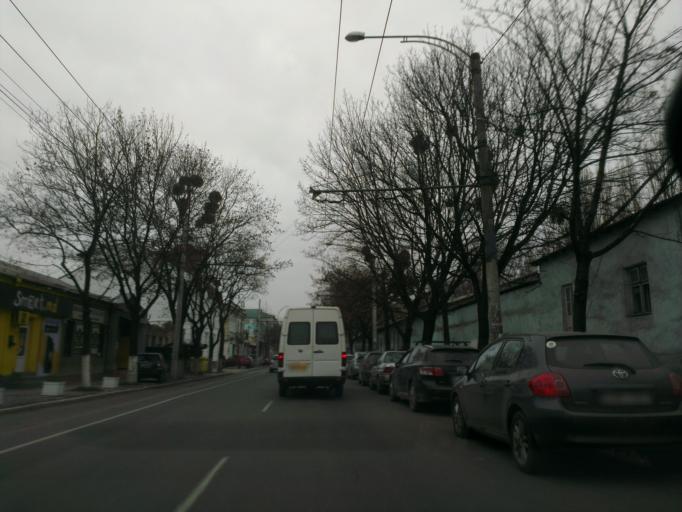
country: MD
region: Chisinau
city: Chisinau
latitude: 47.0142
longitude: 28.8392
